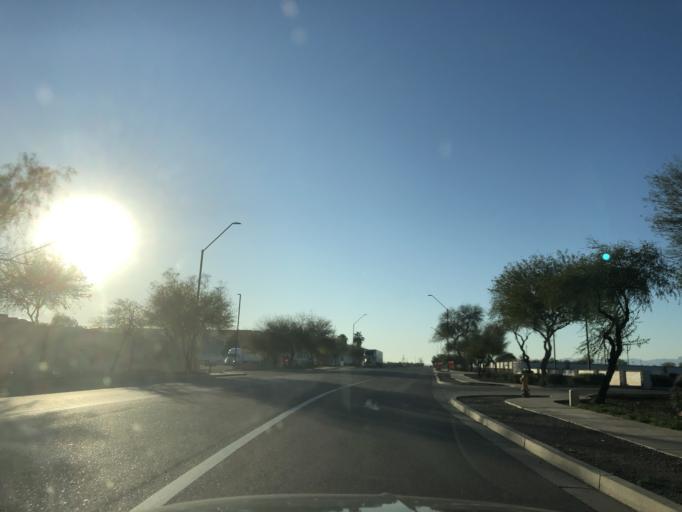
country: US
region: Arizona
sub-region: Maricopa County
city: Tolleson
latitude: 33.4575
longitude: -112.2749
